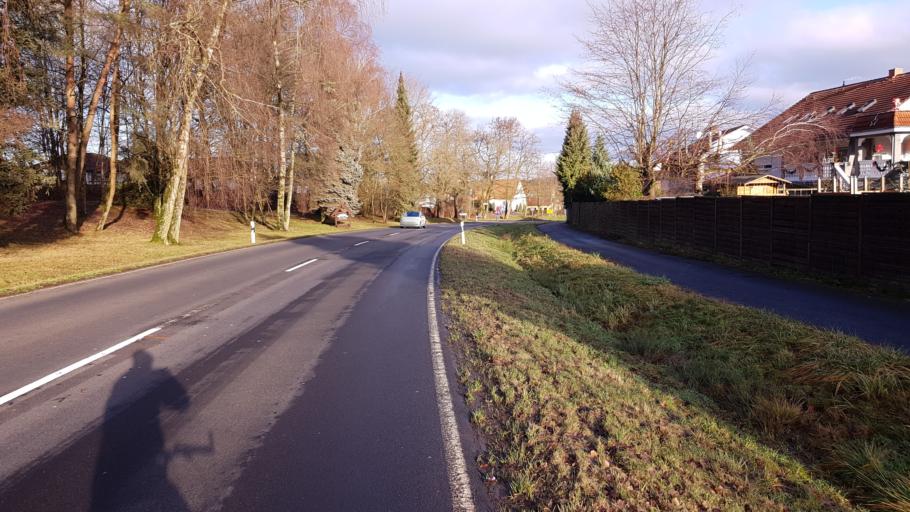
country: DE
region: Hesse
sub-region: Regierungsbezirk Giessen
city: Grunberg
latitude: 50.6418
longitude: 9.0300
